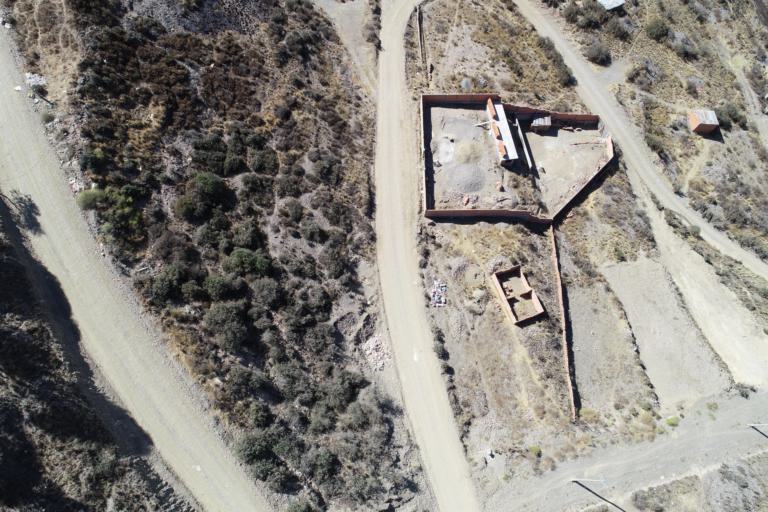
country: BO
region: La Paz
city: La Paz
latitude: -16.5418
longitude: -68.1533
